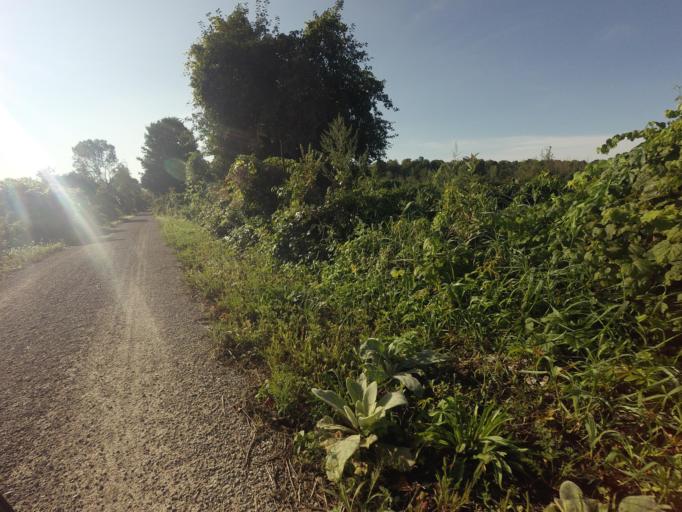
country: CA
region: Ontario
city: Goderich
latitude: 43.7521
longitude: -81.5061
